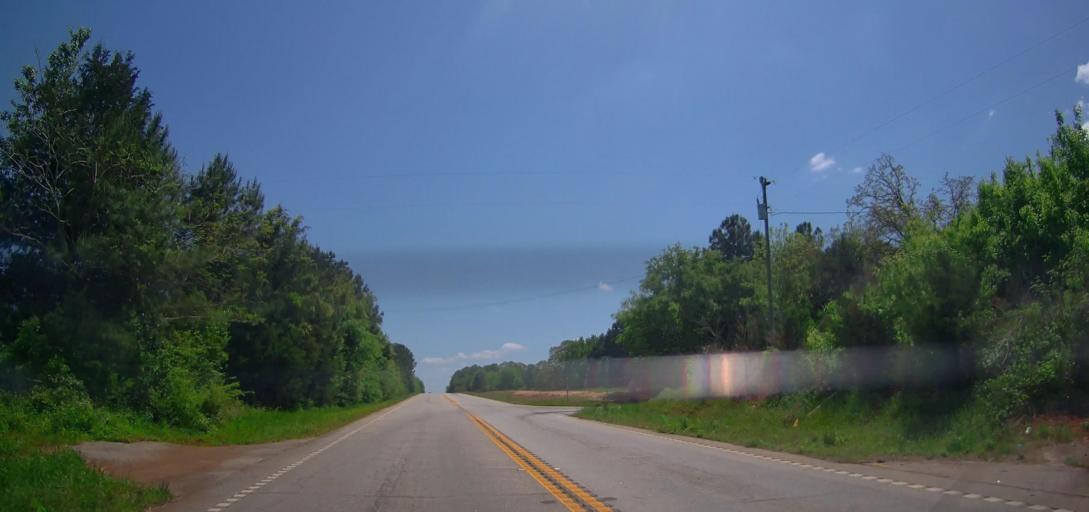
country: US
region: Georgia
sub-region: Jasper County
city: Monticello
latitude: 33.2903
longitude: -83.6777
